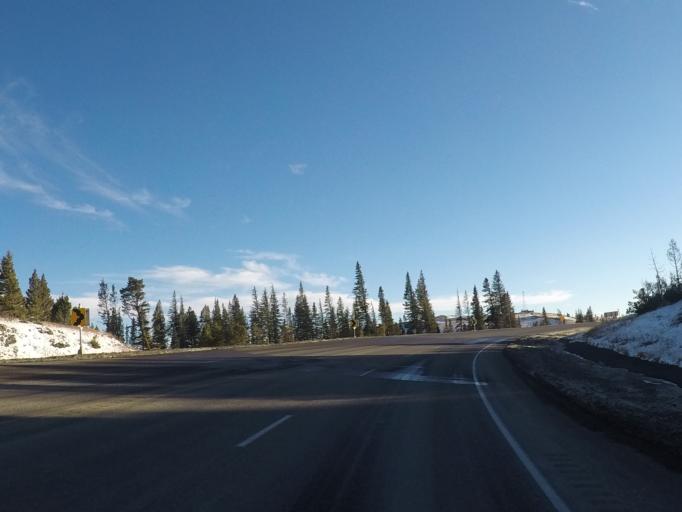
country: US
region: Montana
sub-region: Lewis and Clark County
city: Helena West Side
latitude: 46.5639
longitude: -112.3057
